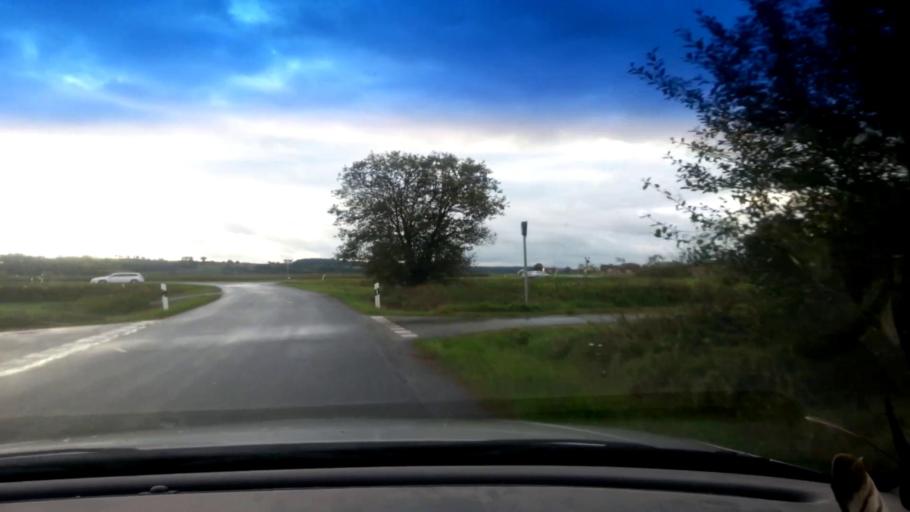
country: DE
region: Bavaria
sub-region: Upper Franconia
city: Burgebrach
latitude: 49.8215
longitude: 10.6768
